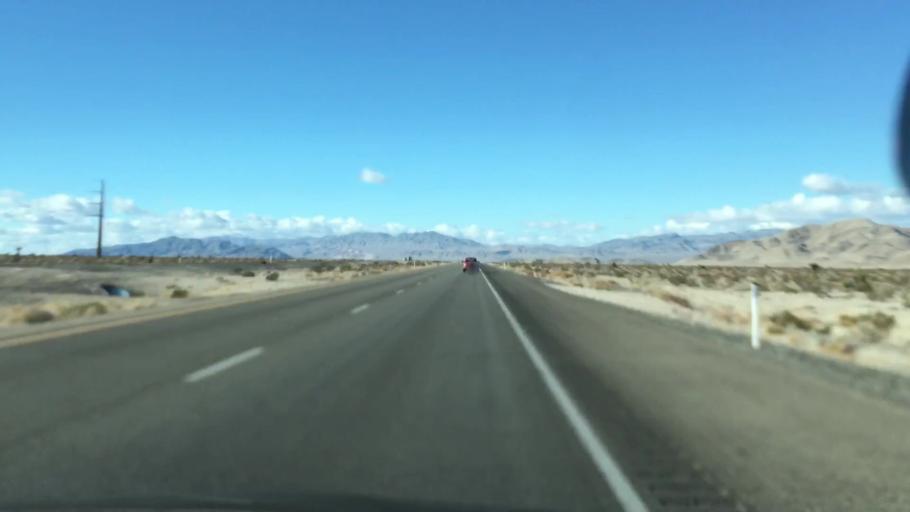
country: US
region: Nevada
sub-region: Nye County
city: Pahrump
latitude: 36.5562
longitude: -115.6039
